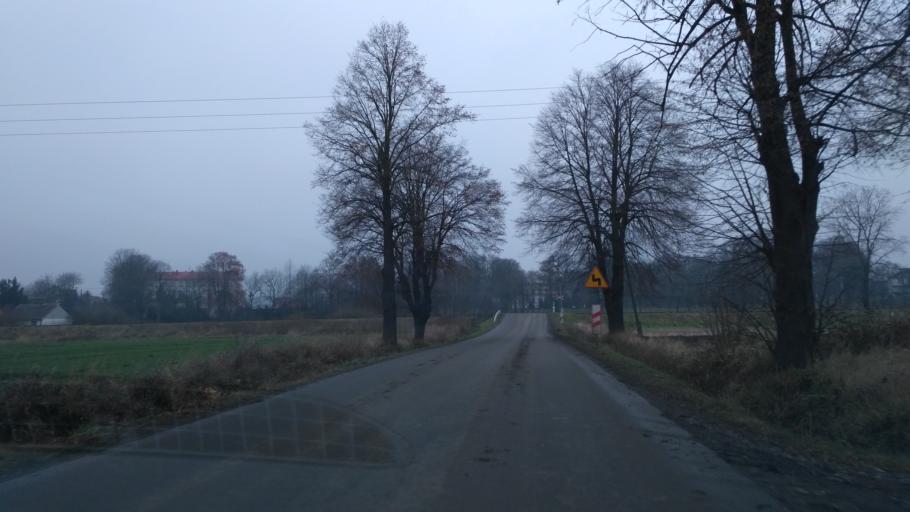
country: PL
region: Subcarpathian Voivodeship
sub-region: Powiat przeworski
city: Urzejowice
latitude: 50.0098
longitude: 22.4690
